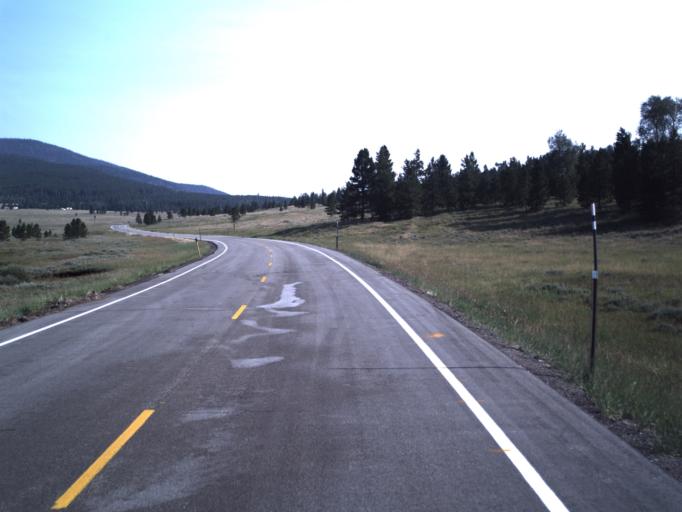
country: US
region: Utah
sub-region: Uintah County
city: Maeser
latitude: 40.7776
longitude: -109.4702
